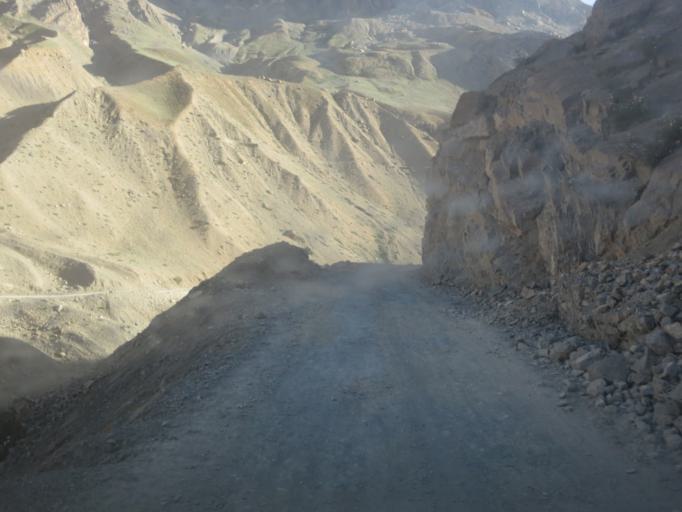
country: IN
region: Himachal Pradesh
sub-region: Kulu
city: Manali
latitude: 32.3279
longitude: 77.9217
